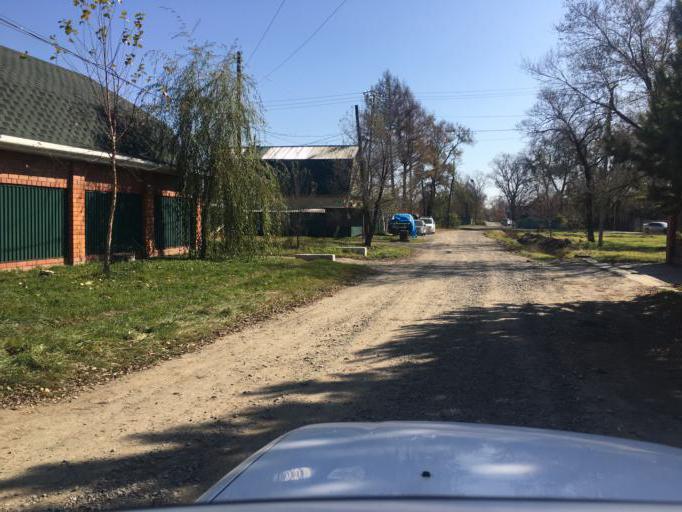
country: RU
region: Primorskiy
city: Dal'nerechensk
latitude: 45.9276
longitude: 133.7350
